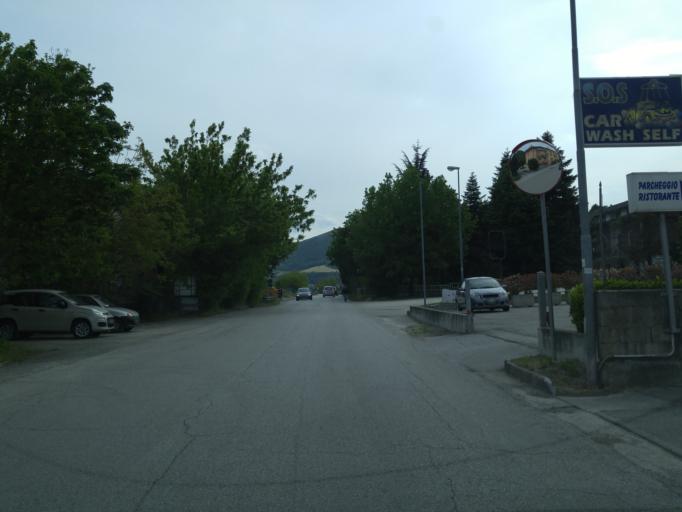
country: IT
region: The Marches
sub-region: Provincia di Pesaro e Urbino
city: Acqualagna
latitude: 43.6283
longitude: 12.6821
